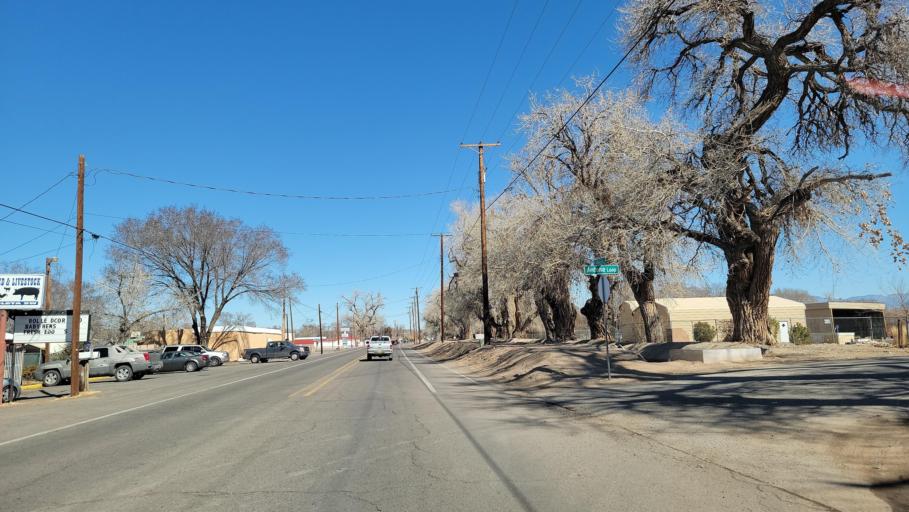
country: US
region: New Mexico
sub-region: Bernalillo County
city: South Valley
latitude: 35.0084
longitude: -106.6883
